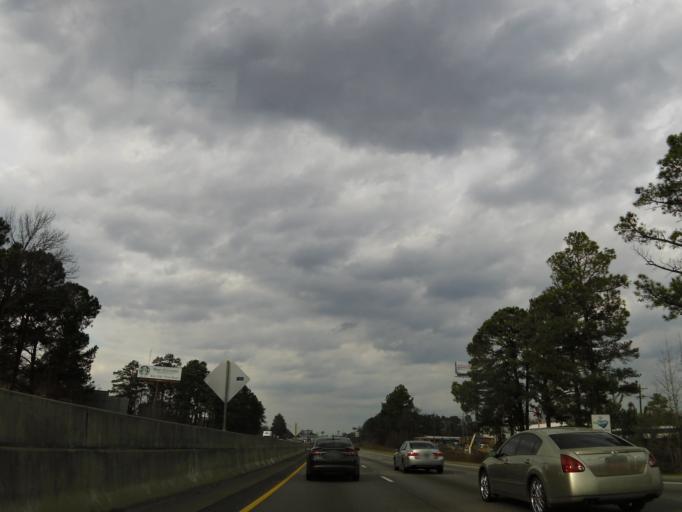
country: US
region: South Carolina
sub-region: Lexington County
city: West Columbia
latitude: 33.9935
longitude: -81.1077
